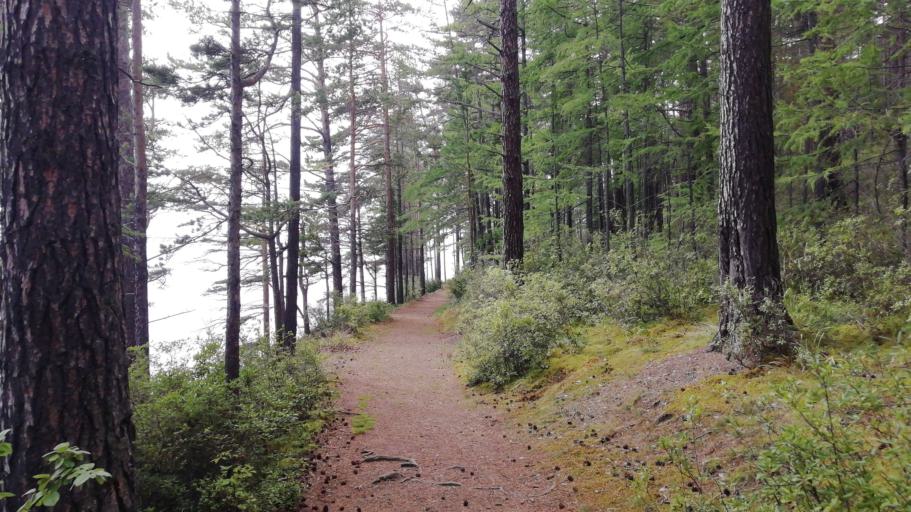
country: RU
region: Irkutsk
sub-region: Irkutskiy Rayon
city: Listvyanka
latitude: 51.8944
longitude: 105.0512
